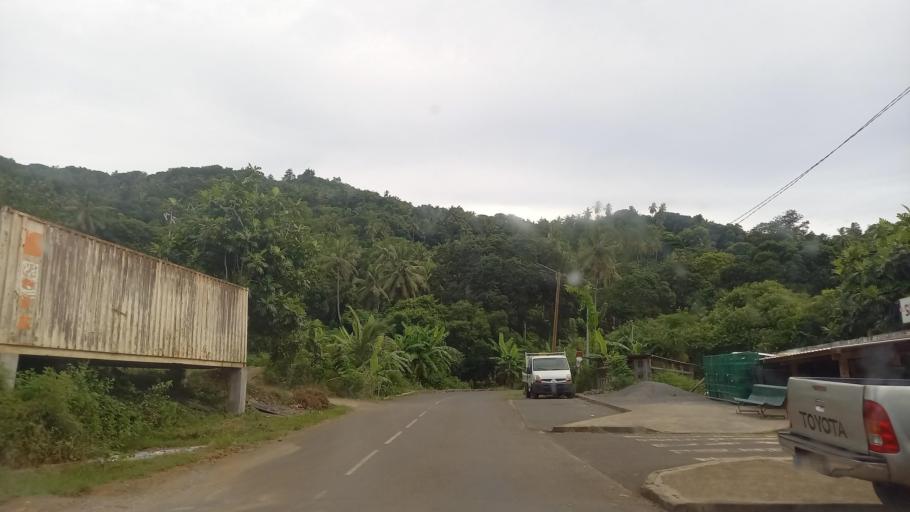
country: YT
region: Boueni
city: Boueni
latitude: -12.9016
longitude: 45.0935
